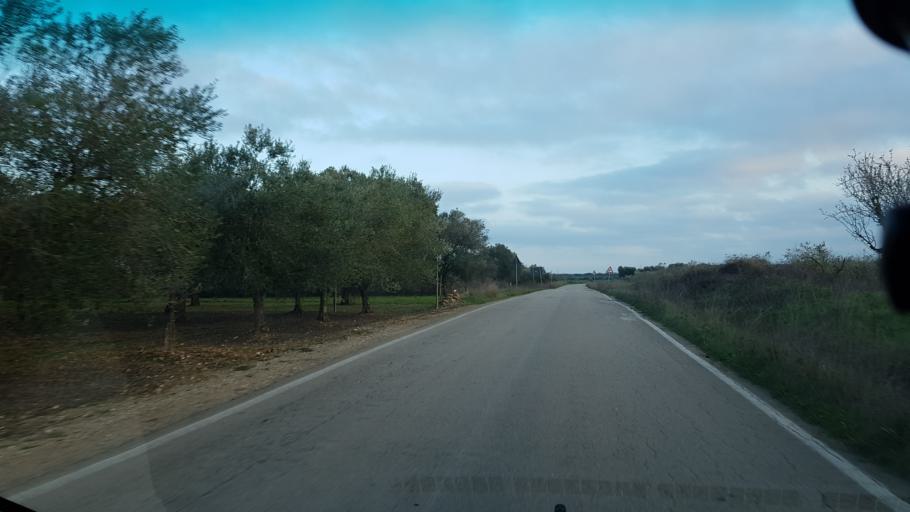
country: IT
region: Apulia
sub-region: Provincia di Brindisi
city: Mesagne
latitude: 40.6188
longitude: 17.7851
